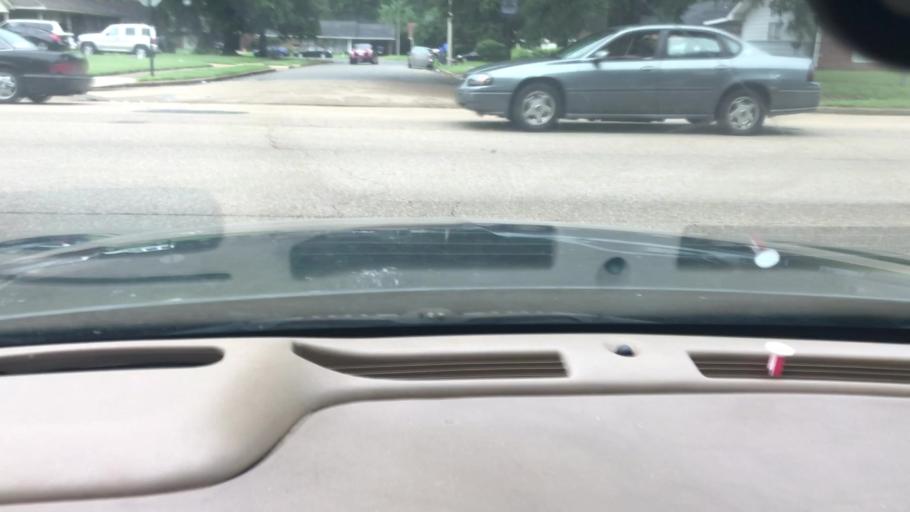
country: US
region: Tennessee
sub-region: Shelby County
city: Germantown
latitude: 35.0621
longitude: -89.8954
